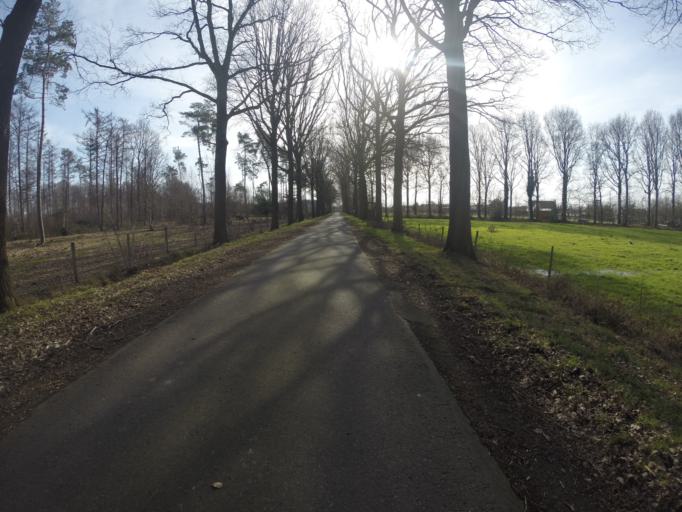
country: BE
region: Flanders
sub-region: Provincie West-Vlaanderen
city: Oostkamp
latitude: 51.1196
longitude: 3.2391
